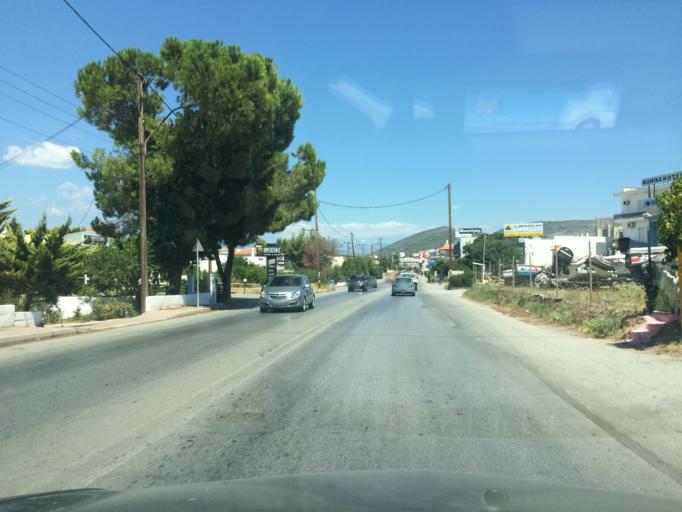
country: GR
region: Central Greece
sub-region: Nomos Evvoias
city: Chalkida
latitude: 38.4795
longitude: 23.6269
